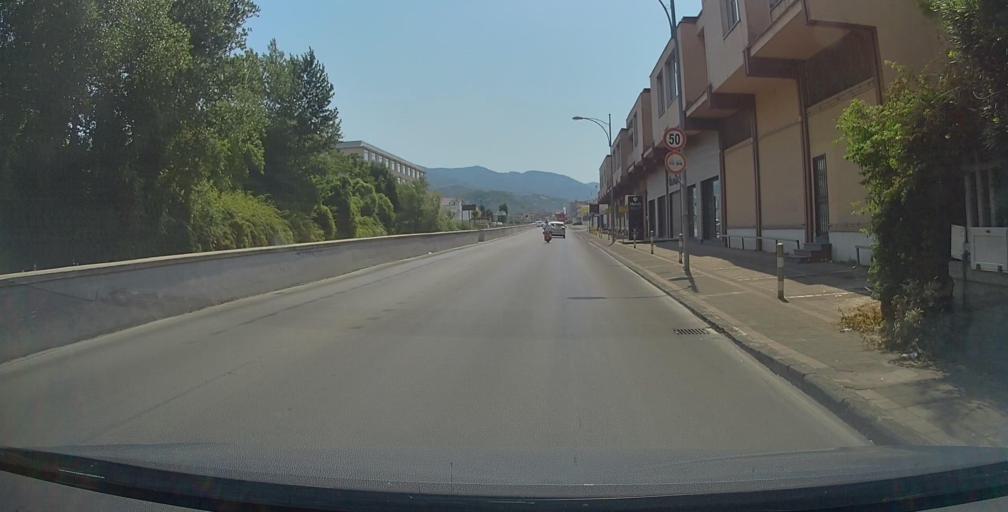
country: IT
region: Campania
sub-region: Provincia di Salerno
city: Nocera Superiore
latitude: 40.7374
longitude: 14.6766
